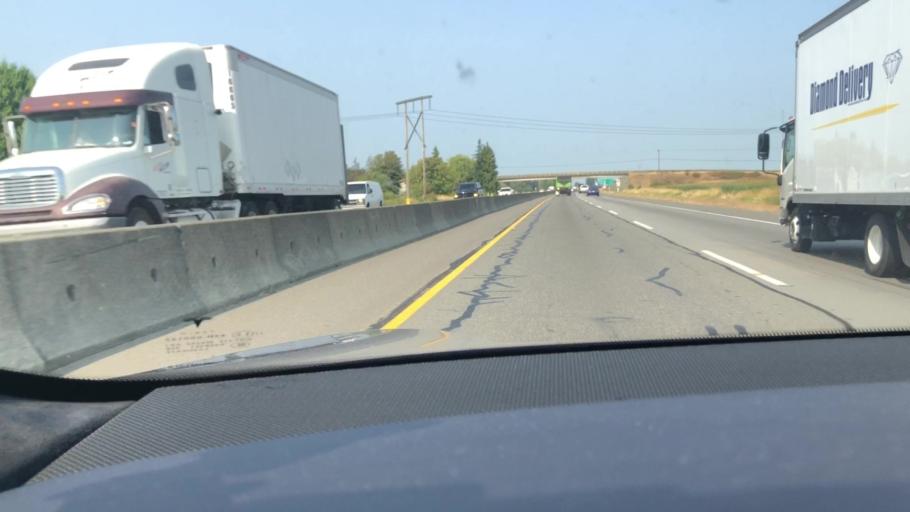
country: CA
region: British Columbia
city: Richmond
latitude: 49.1768
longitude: -123.0427
